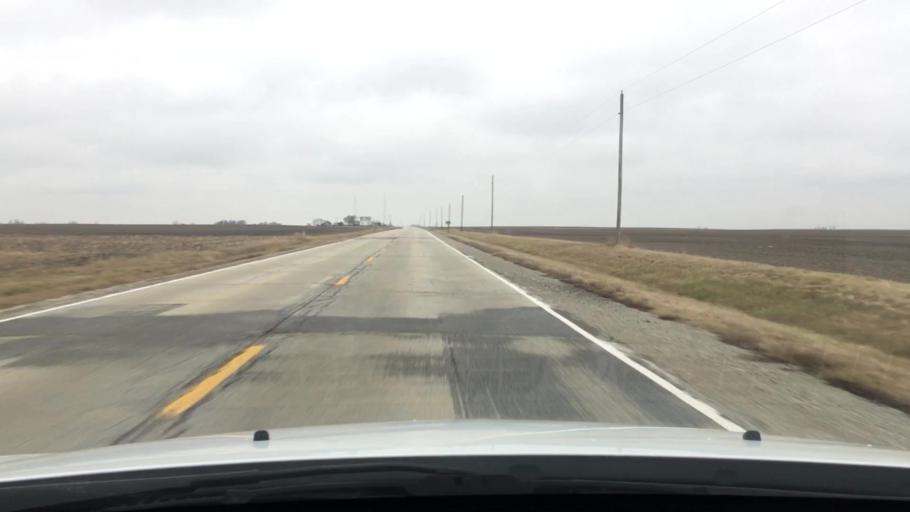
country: US
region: Illinois
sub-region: Iroquois County
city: Clifton
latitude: 40.8838
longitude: -87.9759
